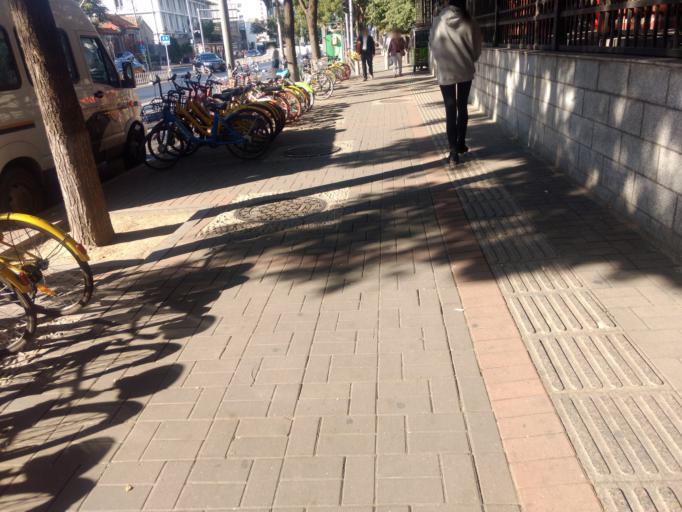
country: CN
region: Beijing
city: Beijing
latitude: 39.8953
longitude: 116.3783
